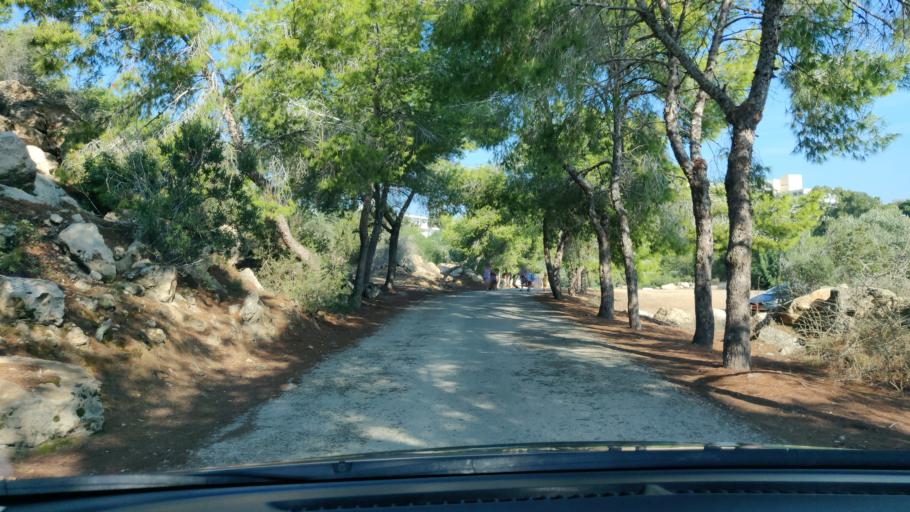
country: CY
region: Ammochostos
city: Protaras
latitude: 34.9823
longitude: 34.0680
